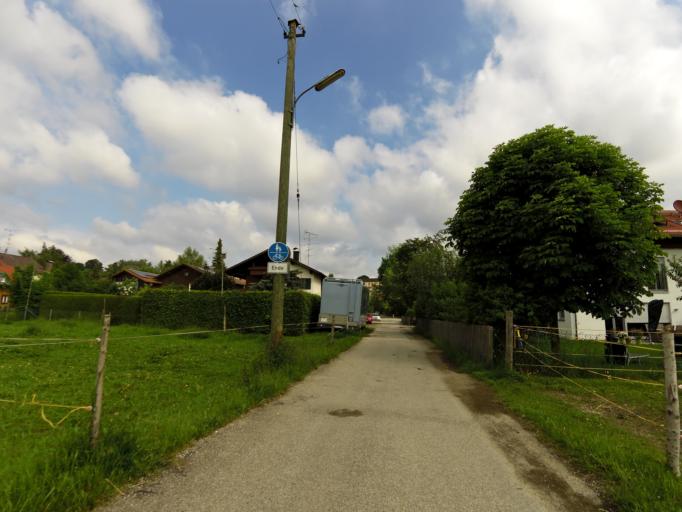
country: DE
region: Bavaria
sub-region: Upper Bavaria
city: Schaftlarn
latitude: 47.9889
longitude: 11.4542
